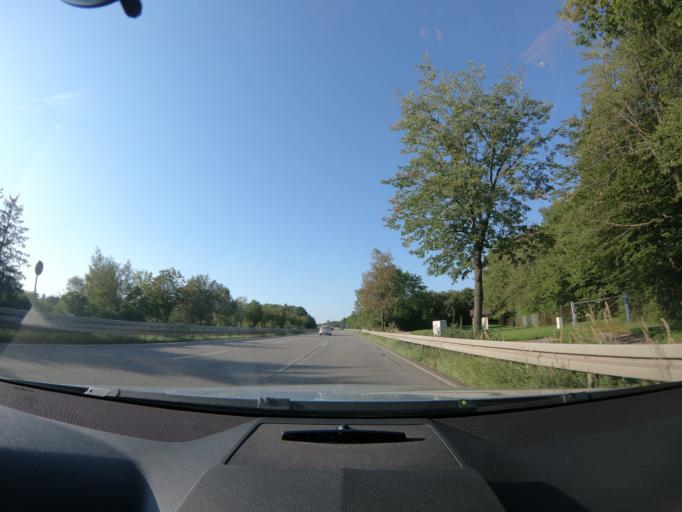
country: DE
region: Bavaria
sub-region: Upper Bavaria
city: Oberschleissheim
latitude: 48.2220
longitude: 11.5878
